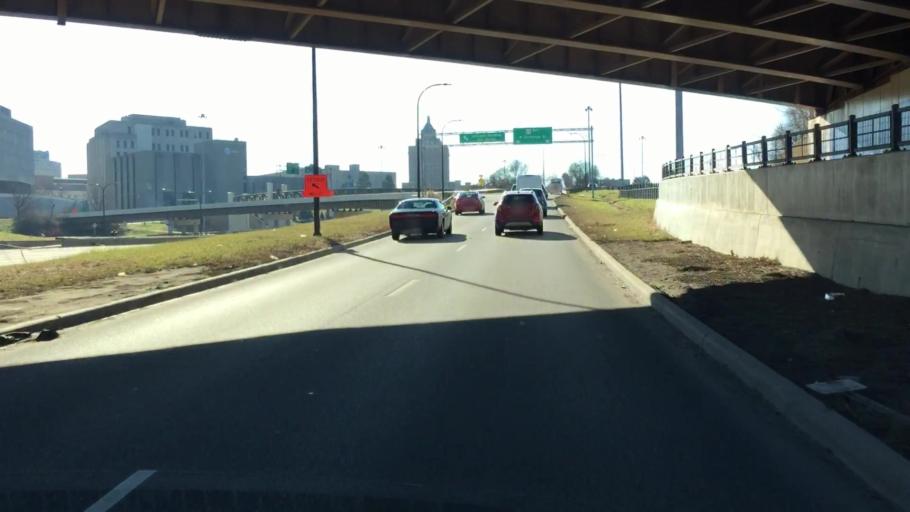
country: US
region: Ohio
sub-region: Summit County
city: Akron
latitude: 41.0852
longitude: -81.5202
